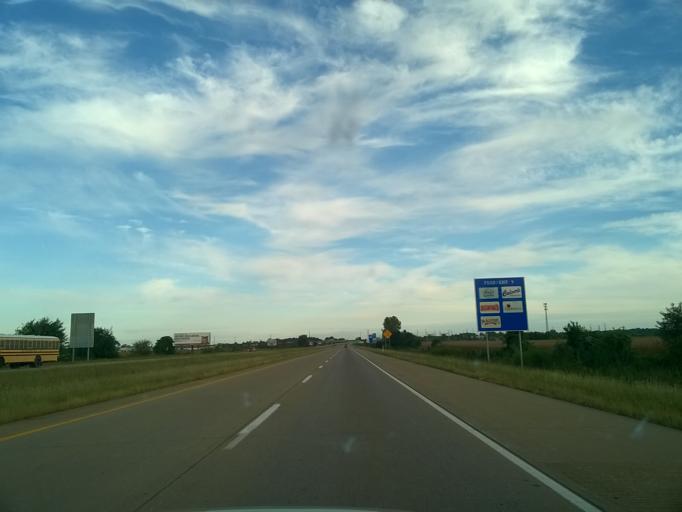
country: US
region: Indiana
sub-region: Warrick County
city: Newburgh
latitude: 37.9855
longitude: -87.4581
